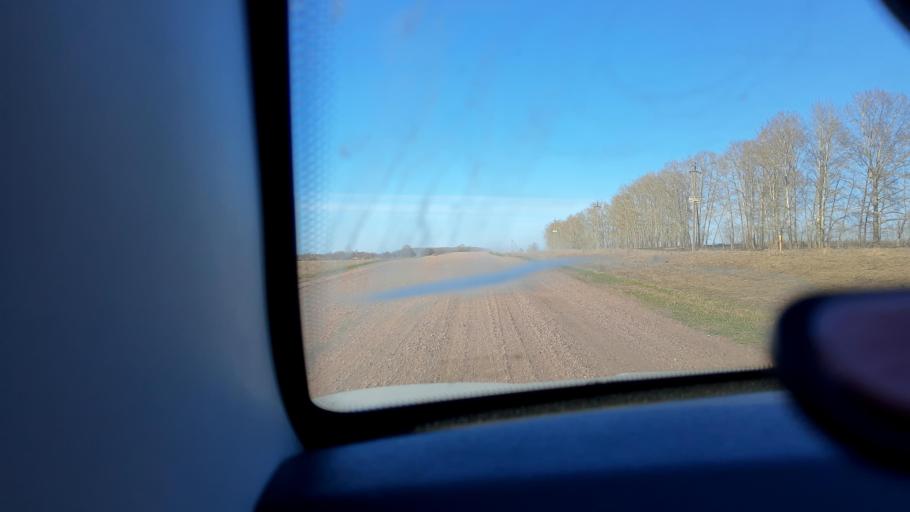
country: RU
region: Bashkortostan
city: Asanovo
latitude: 54.8766
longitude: 55.4716
